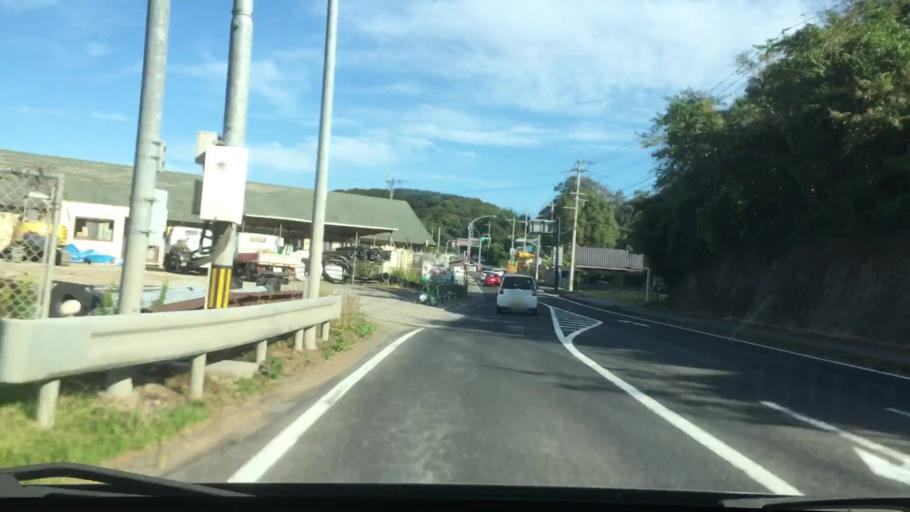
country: JP
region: Nagasaki
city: Sasebo
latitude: 33.0646
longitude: 129.7642
